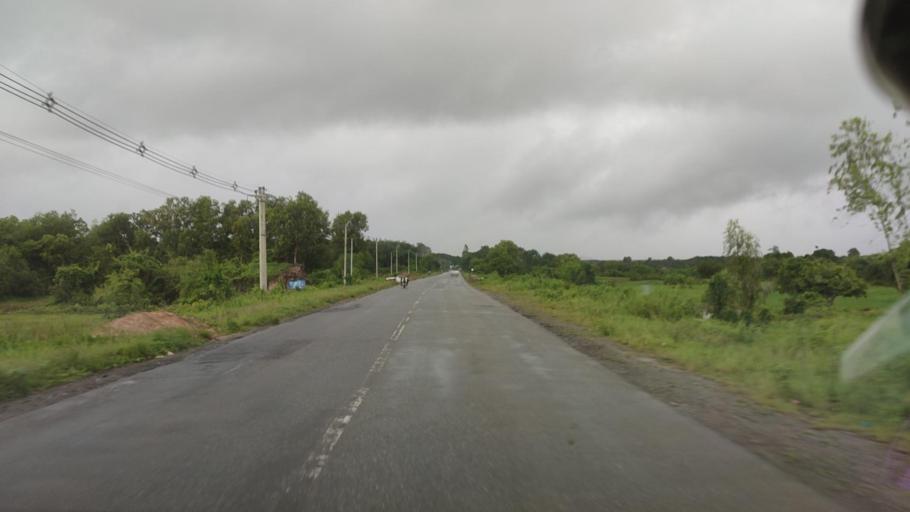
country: MM
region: Bago
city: Bago
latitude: 17.3642
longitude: 96.4597
